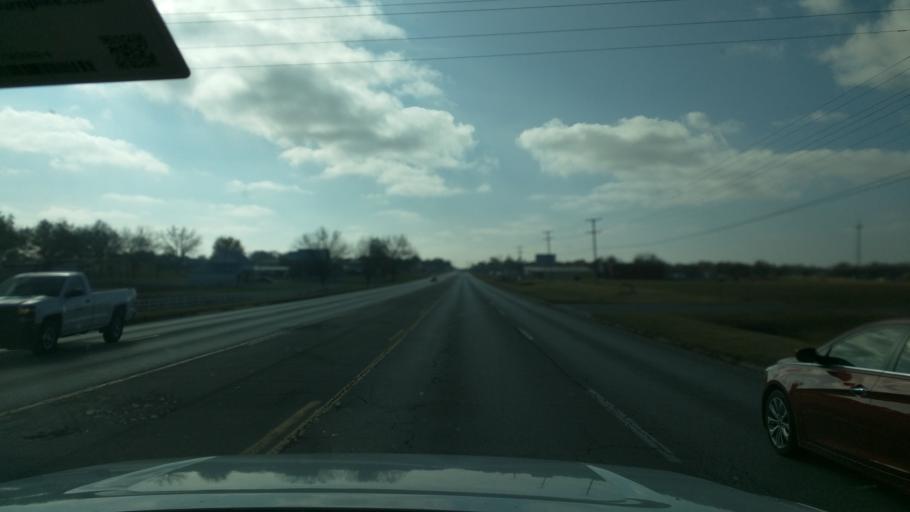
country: US
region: Oklahoma
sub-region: Washington County
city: Dewey
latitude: 36.7786
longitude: -95.9355
